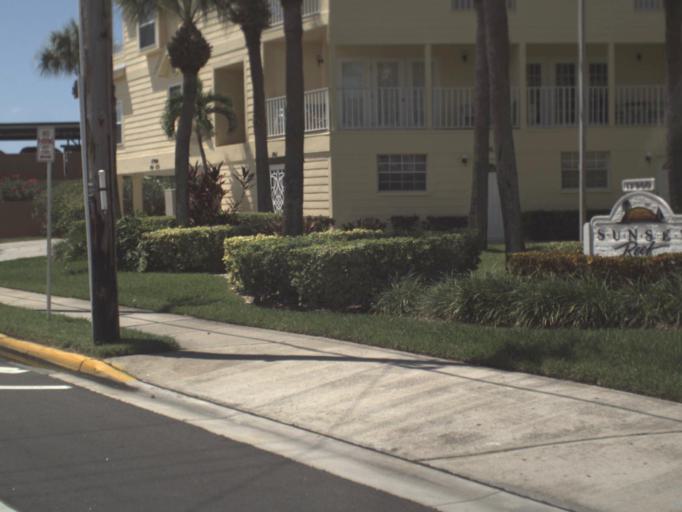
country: US
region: Florida
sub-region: Pinellas County
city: Redington Shores
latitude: 27.8315
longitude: -82.8322
